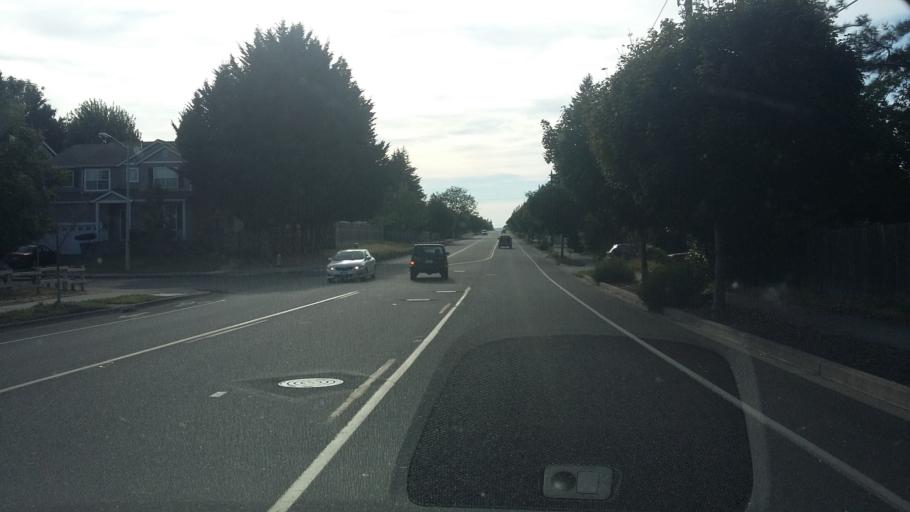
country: US
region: Washington
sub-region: Clark County
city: Walnut Grove
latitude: 45.6678
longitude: -122.5869
